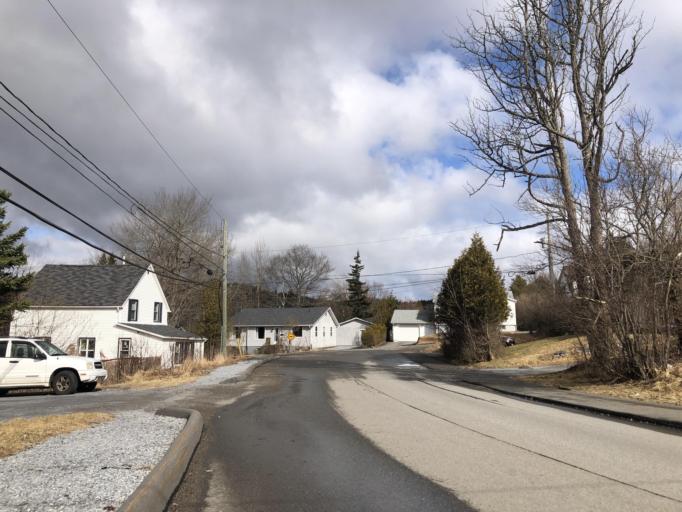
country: CA
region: New Brunswick
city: Saint John
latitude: 45.3220
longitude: -66.0109
